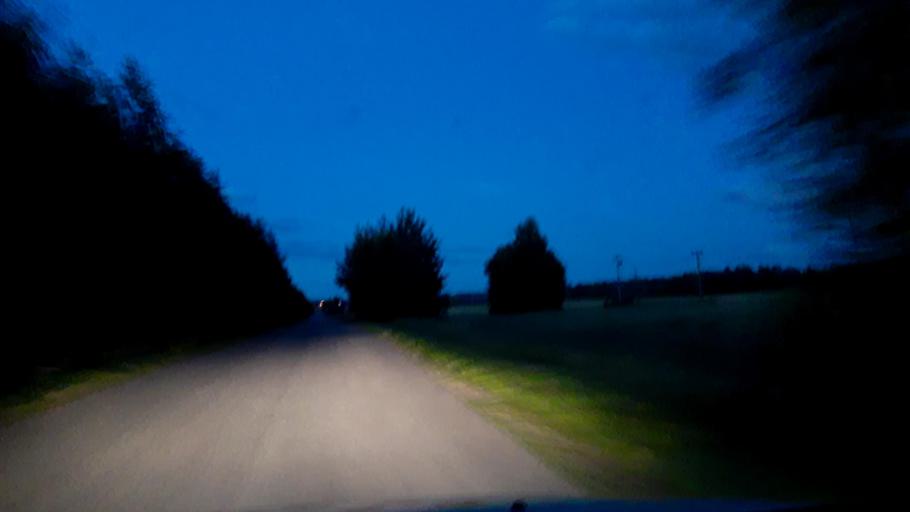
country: RU
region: Nizjnij Novgorod
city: Pamyat' Parizhskoy Kommuny
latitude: 56.0595
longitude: 44.4770
